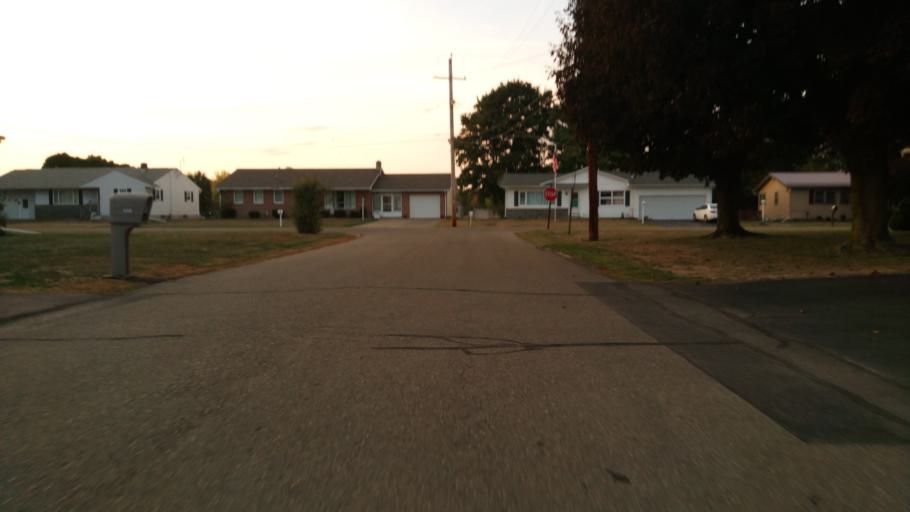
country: US
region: New York
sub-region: Chemung County
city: Southport
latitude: 42.0607
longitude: -76.7826
